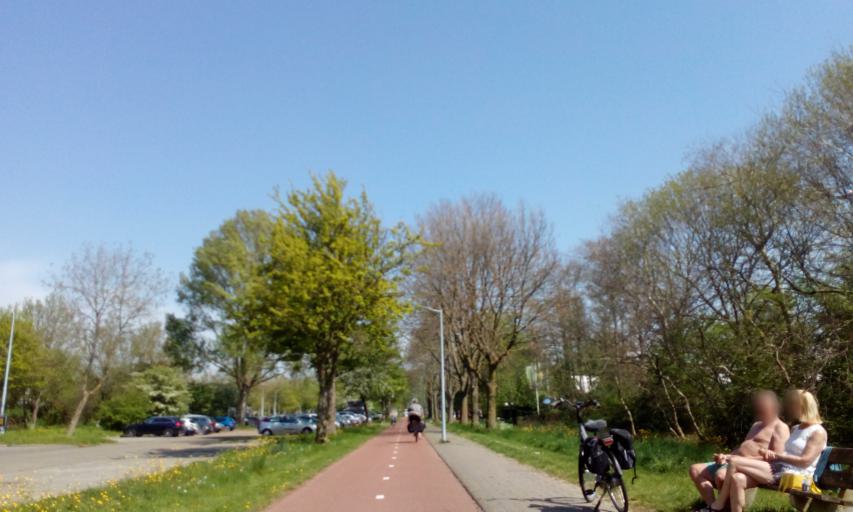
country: NL
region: South Holland
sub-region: Gemeente Kaag en Braassem
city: Oude Wetering
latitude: 52.2582
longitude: 4.6393
